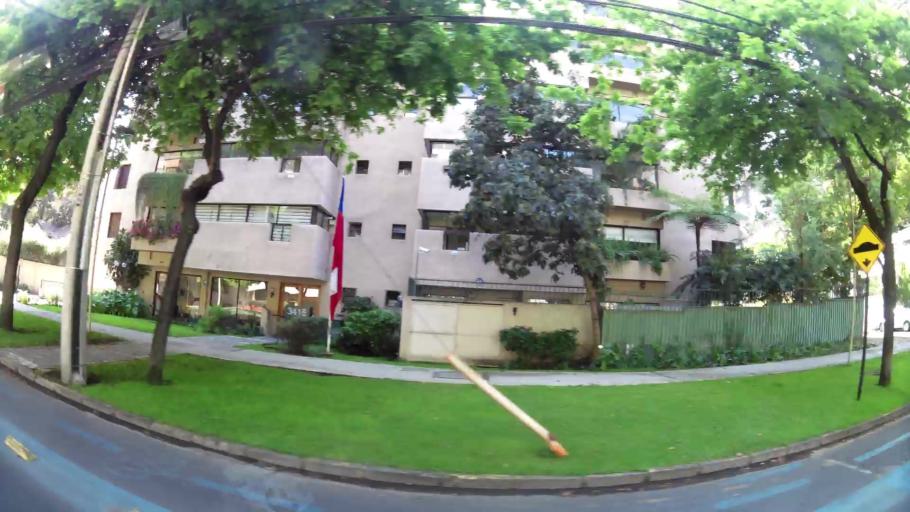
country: CL
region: Santiago Metropolitan
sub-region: Provincia de Santiago
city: Villa Presidente Frei, Nunoa, Santiago, Chile
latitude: -33.4183
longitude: -70.5936
